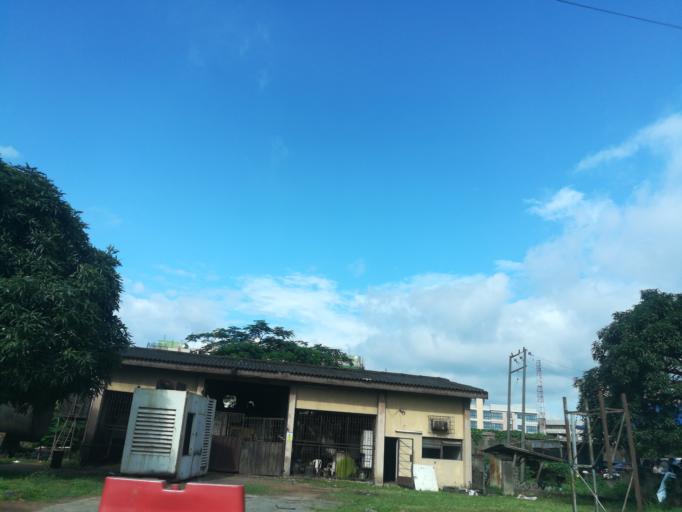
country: NG
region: Lagos
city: Ikeja
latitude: 6.6165
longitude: 3.3552
